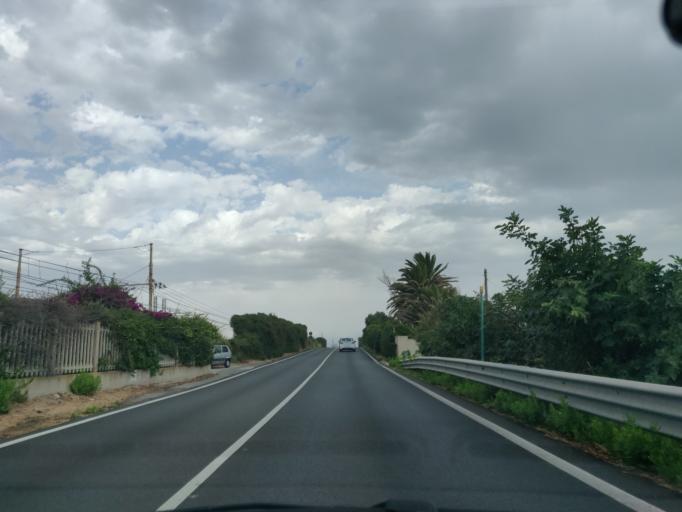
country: IT
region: Latium
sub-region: Citta metropolitana di Roma Capitale
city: Santa Marinella
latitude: 42.0405
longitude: 11.9126
